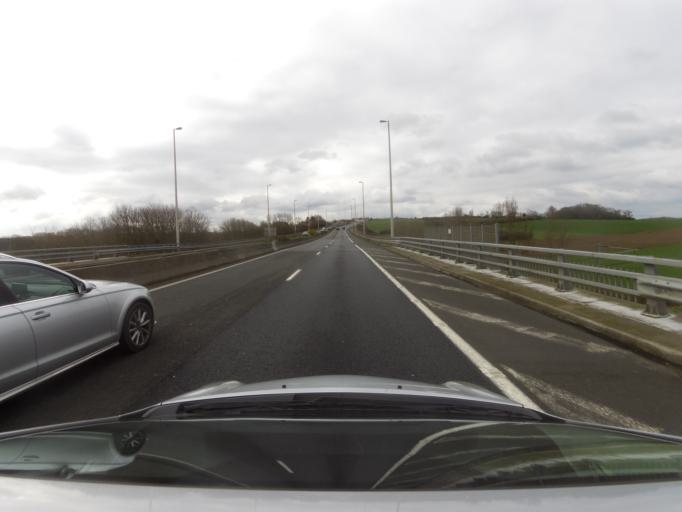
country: FR
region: Nord-Pas-de-Calais
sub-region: Departement du Pas-de-Calais
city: Marquise
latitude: 50.7996
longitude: 1.6897
